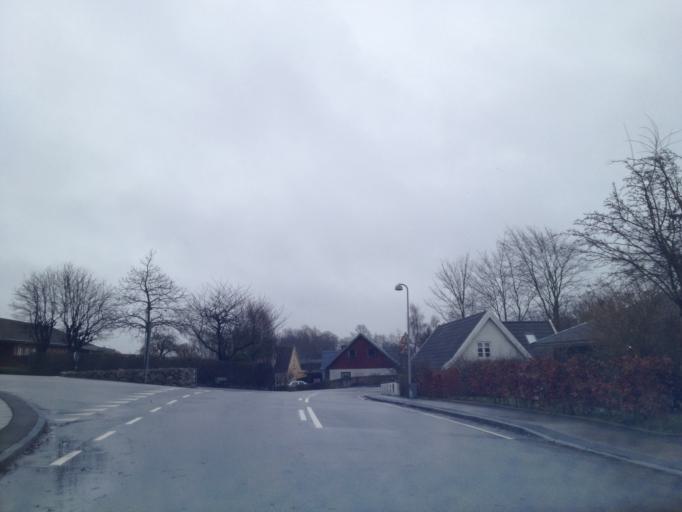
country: DK
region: Capital Region
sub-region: Hoje-Taastrup Kommune
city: Flong
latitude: 55.6610
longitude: 12.1809
